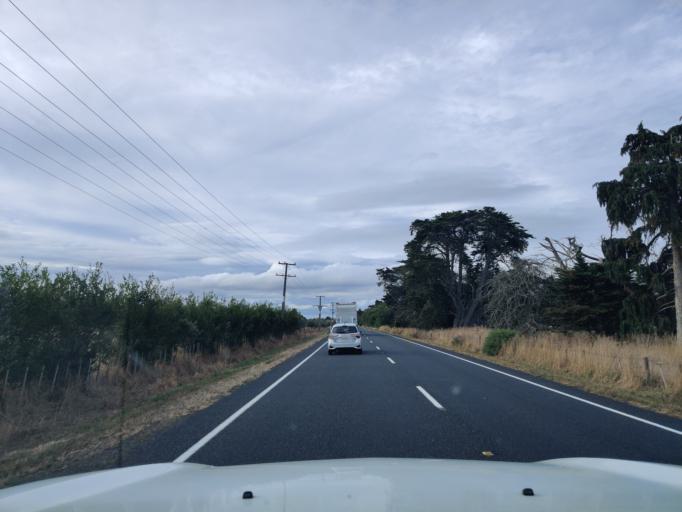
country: NZ
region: Waikato
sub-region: Hamilton City
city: Hamilton
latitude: -37.6958
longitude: 175.3382
